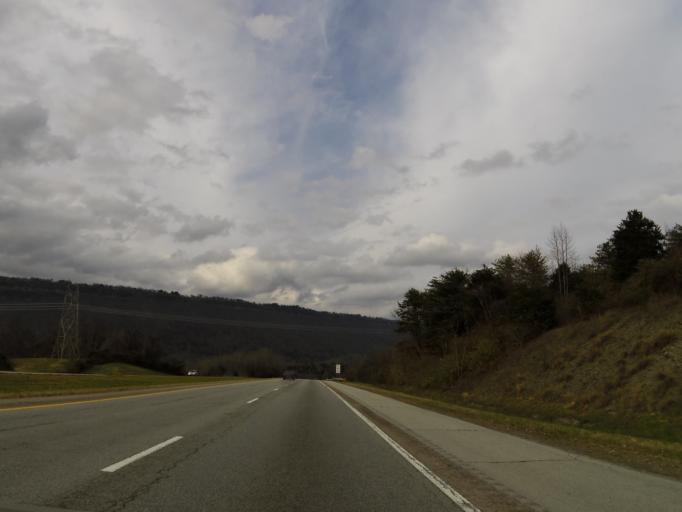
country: US
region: Tennessee
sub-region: Hamilton County
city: Red Bank
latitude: 35.1333
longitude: -85.2936
